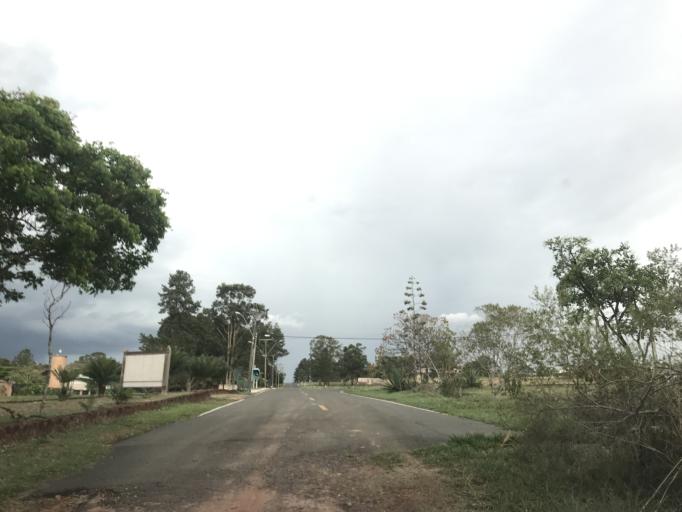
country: BR
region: Federal District
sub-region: Brasilia
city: Brasilia
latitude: -15.9056
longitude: -47.9143
